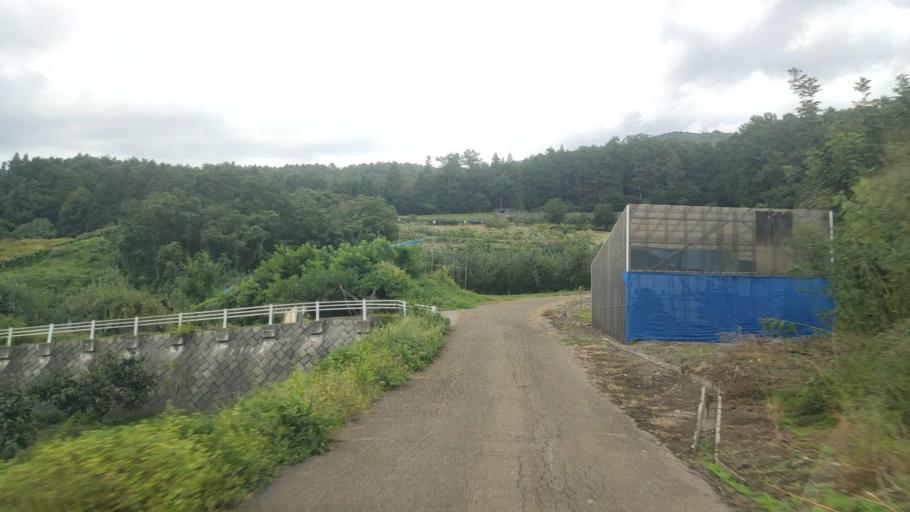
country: JP
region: Nagano
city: Nakano
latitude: 36.7791
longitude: 138.3875
